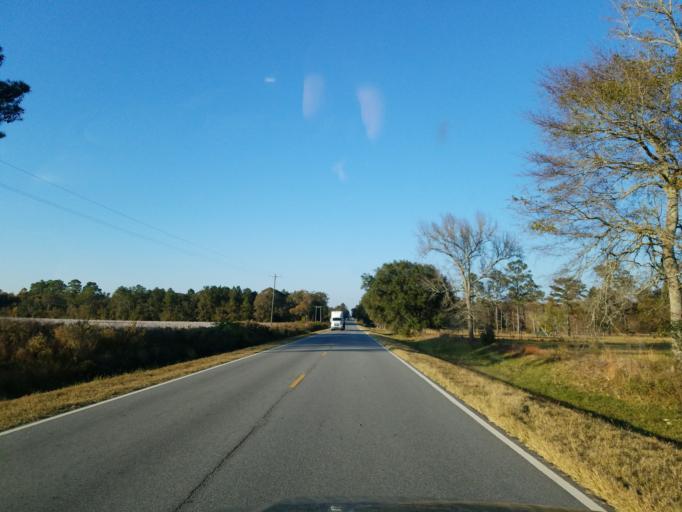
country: US
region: Georgia
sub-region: Lanier County
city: Lakeland
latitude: 31.1338
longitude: -83.0859
